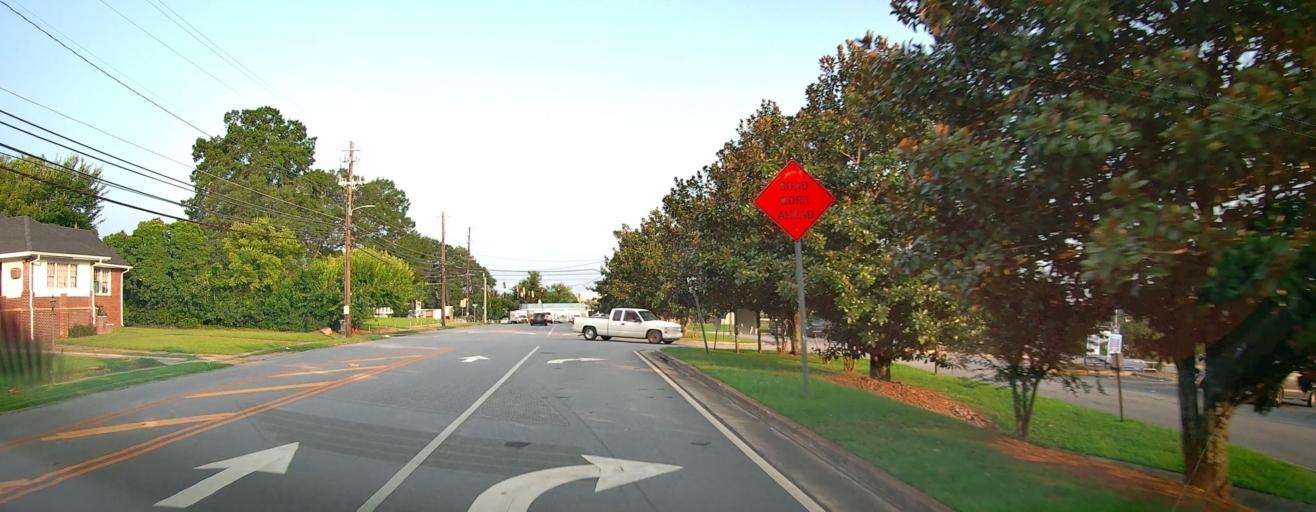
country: US
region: Georgia
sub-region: Bibb County
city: Macon
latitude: 32.8506
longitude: -83.6251
